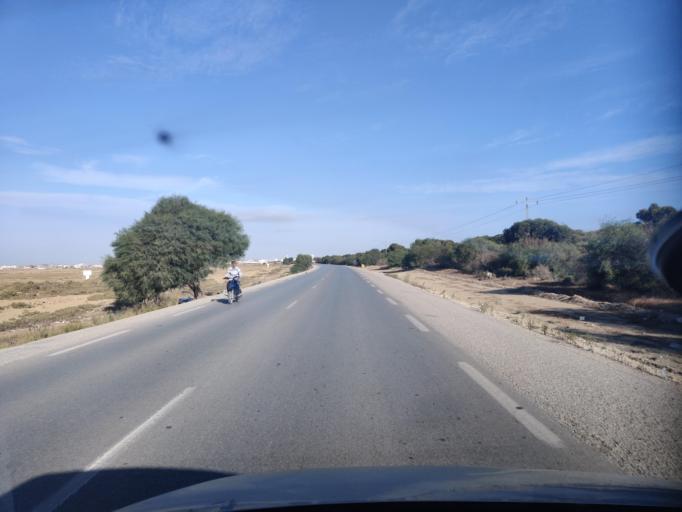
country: TN
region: Ariana
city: Ariana
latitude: 36.9481
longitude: 10.2403
